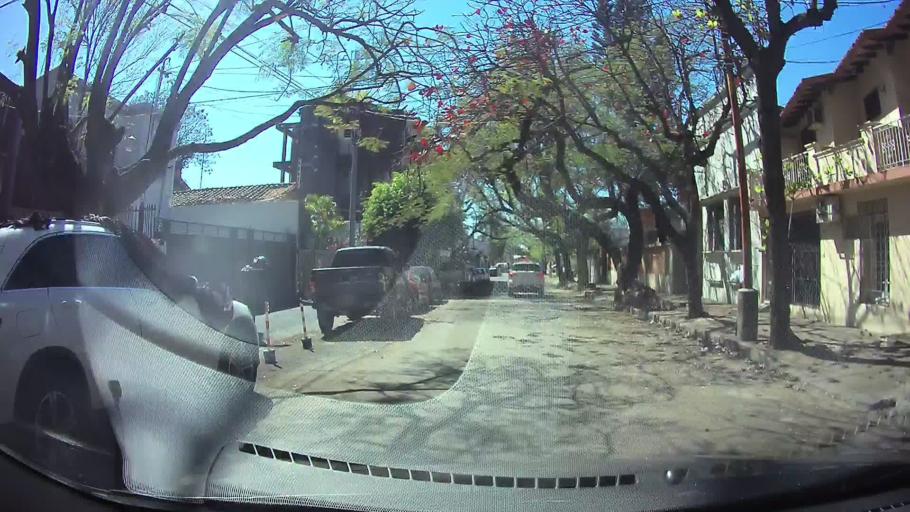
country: PY
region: Asuncion
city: Asuncion
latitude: -25.2833
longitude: -57.6143
